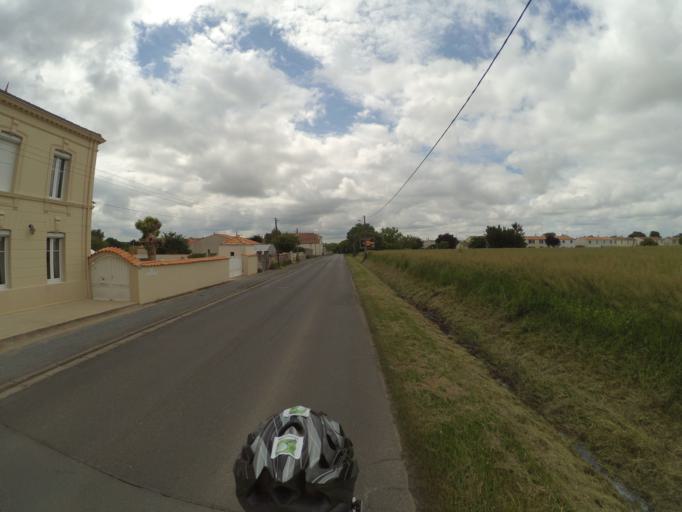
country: FR
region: Poitou-Charentes
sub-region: Departement de la Charente-Maritime
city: Breuil-Magne
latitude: 45.9603
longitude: -0.9698
